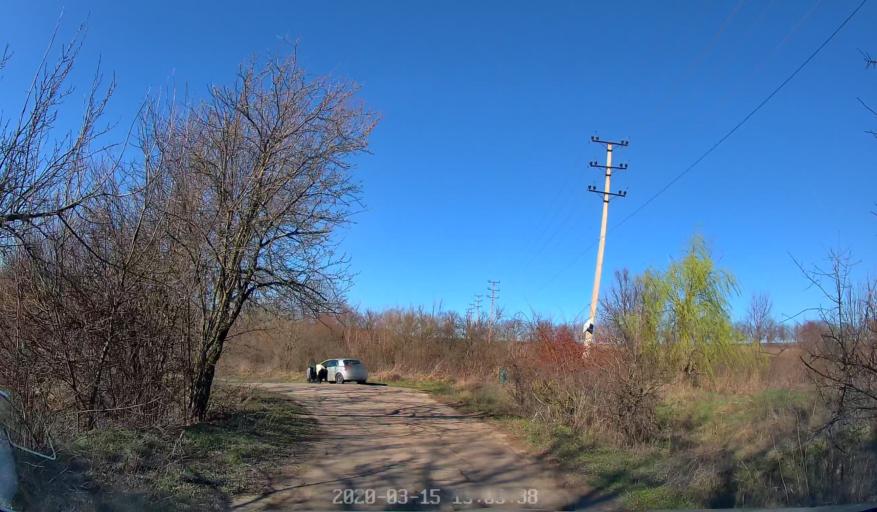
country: MD
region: Orhei
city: Orhei
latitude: 47.2822
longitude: 28.8327
